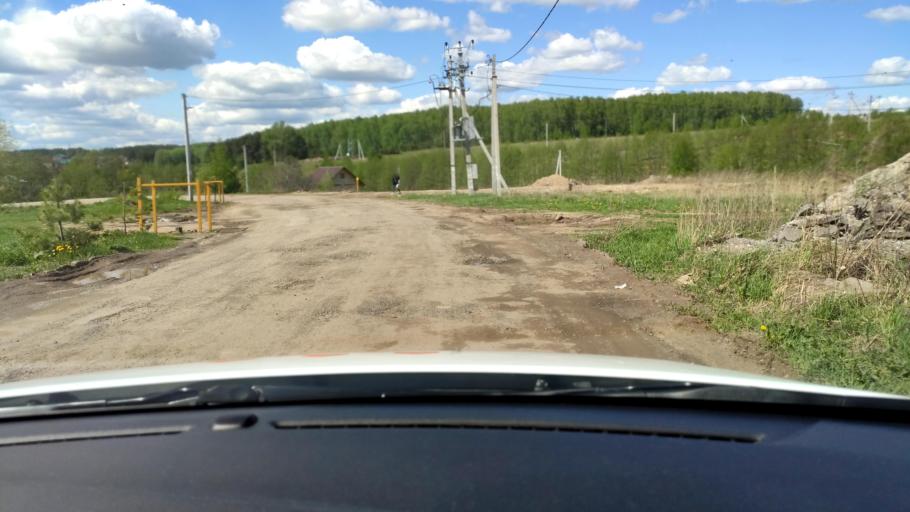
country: RU
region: Tatarstan
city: Vysokaya Gora
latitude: 55.8189
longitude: 49.2834
